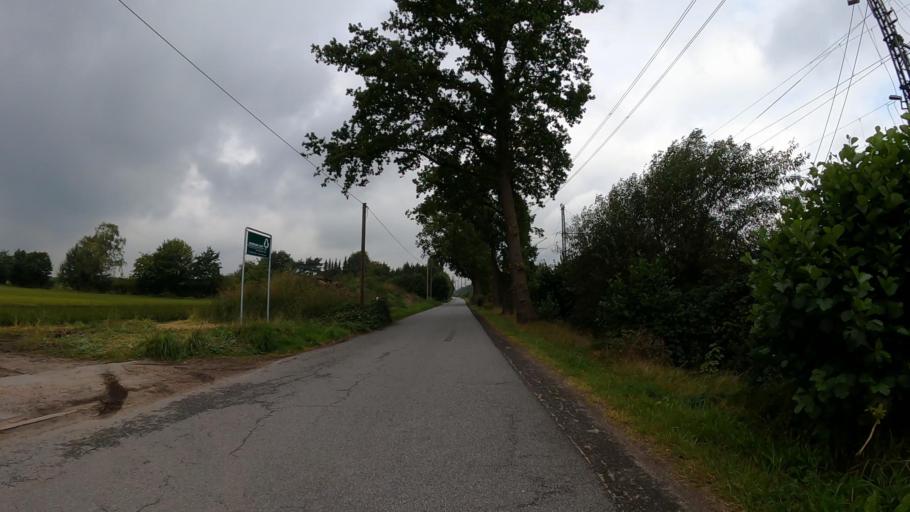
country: DE
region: Schleswig-Holstein
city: Halstenbek
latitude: 53.6210
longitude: 9.8569
